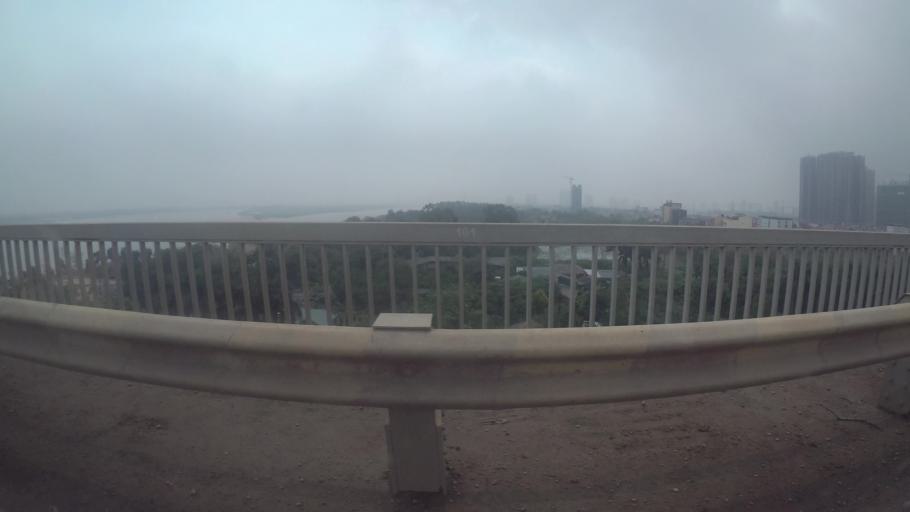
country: VN
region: Ha Noi
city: Tay Ho
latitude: 21.0927
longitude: 105.7861
